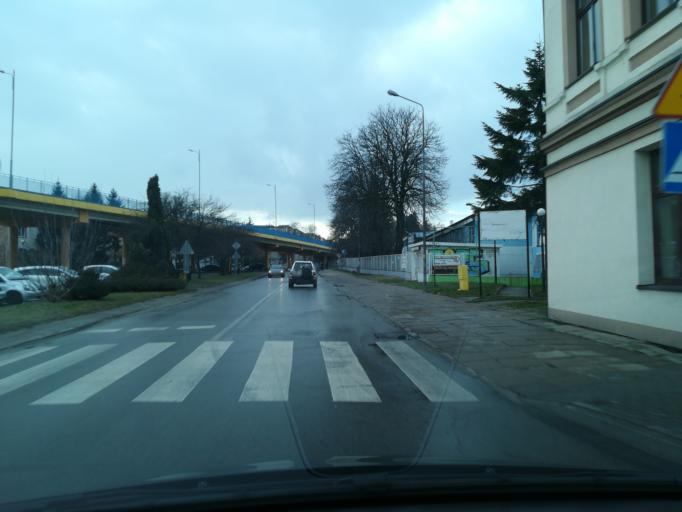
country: PL
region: Lodz Voivodeship
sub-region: Powiat radomszczanski
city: Radomsko
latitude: 51.0692
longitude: 19.4362
